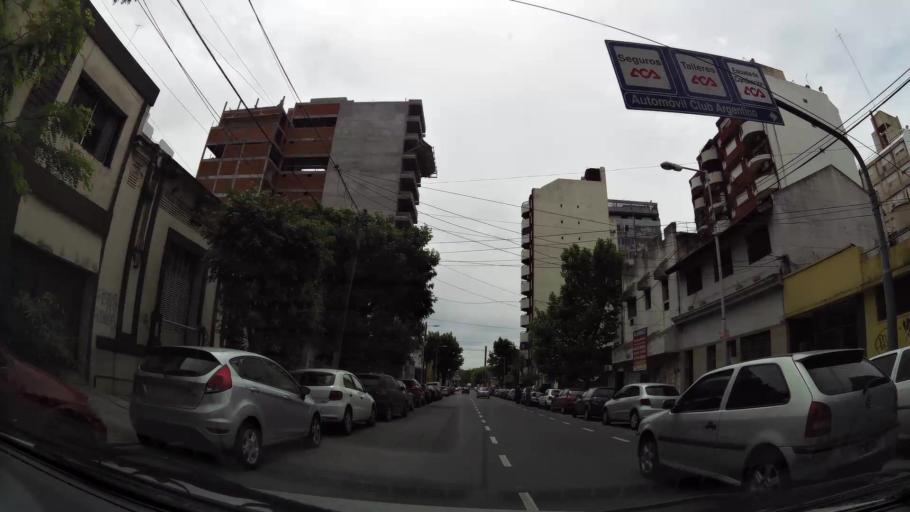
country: AR
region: Buenos Aires
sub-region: Partido de Avellaneda
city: Avellaneda
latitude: -34.6661
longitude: -58.3607
